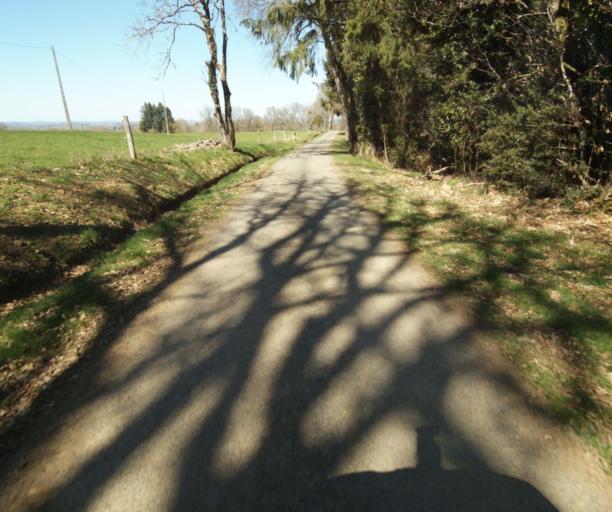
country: FR
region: Limousin
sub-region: Departement de la Correze
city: Chamboulive
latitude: 45.3988
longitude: 1.6805
